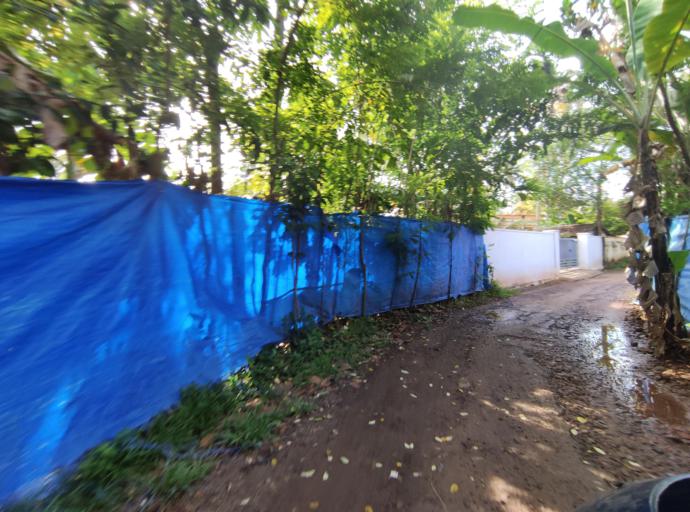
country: IN
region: Kerala
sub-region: Alappuzha
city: Vayalar
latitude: 9.6939
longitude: 76.3346
